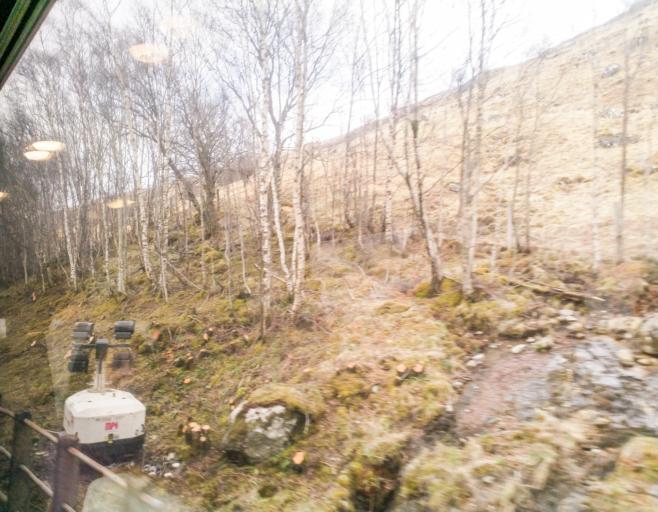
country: GB
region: Scotland
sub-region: Highland
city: Spean Bridge
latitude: 56.7968
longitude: -4.7230
